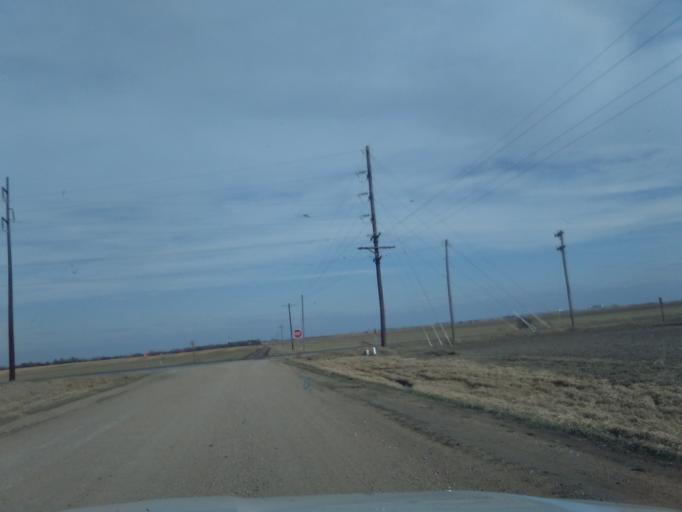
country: US
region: Nebraska
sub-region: Jefferson County
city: Fairbury
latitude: 40.2193
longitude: -97.1807
